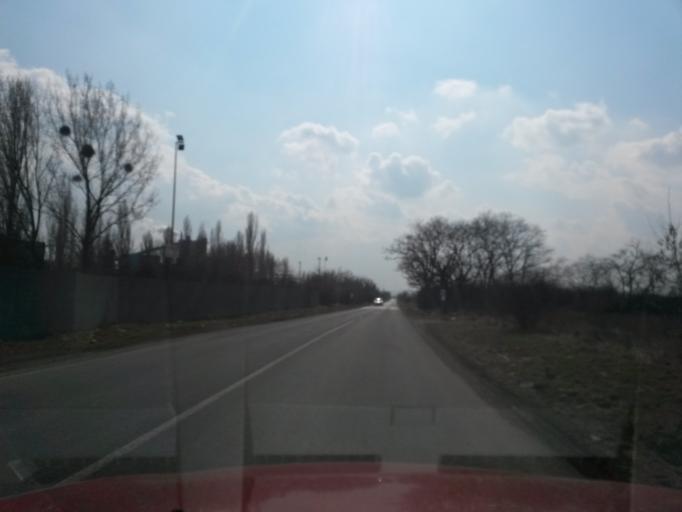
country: SK
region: Kosicky
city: Kosice
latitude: 48.6163
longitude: 21.1792
